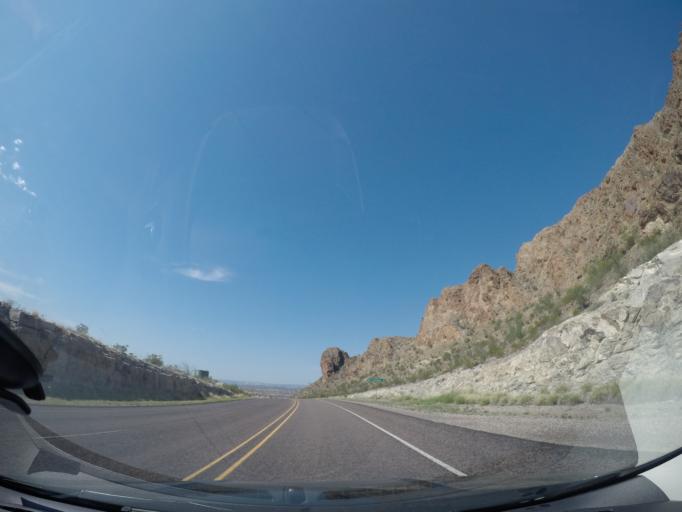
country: US
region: Texas
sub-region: Presidio County
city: Presidio
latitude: 29.3420
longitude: -103.5315
